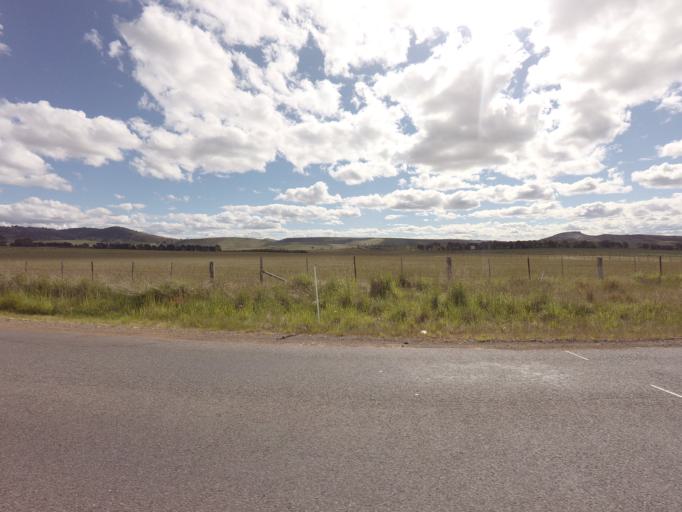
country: AU
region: Tasmania
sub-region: Brighton
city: Bridgewater
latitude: -42.3853
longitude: 147.3147
